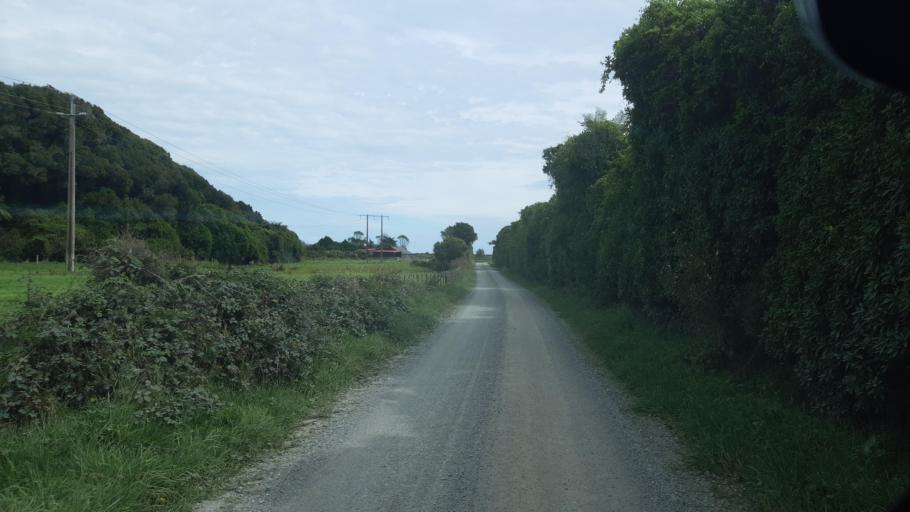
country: NZ
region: West Coast
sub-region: Westland District
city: Hokitika
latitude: -42.9083
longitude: 170.7607
